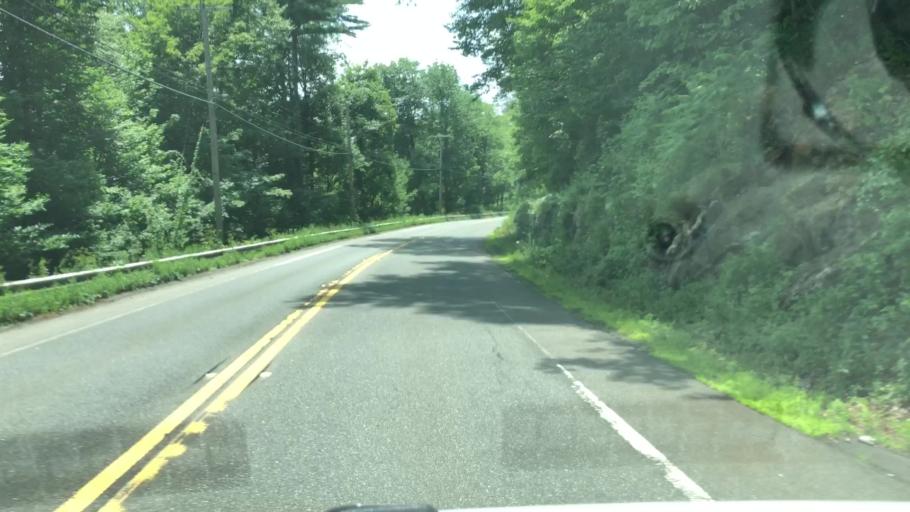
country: US
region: Massachusetts
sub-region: Hampshire County
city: Williamsburg
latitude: 42.4115
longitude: -72.7587
